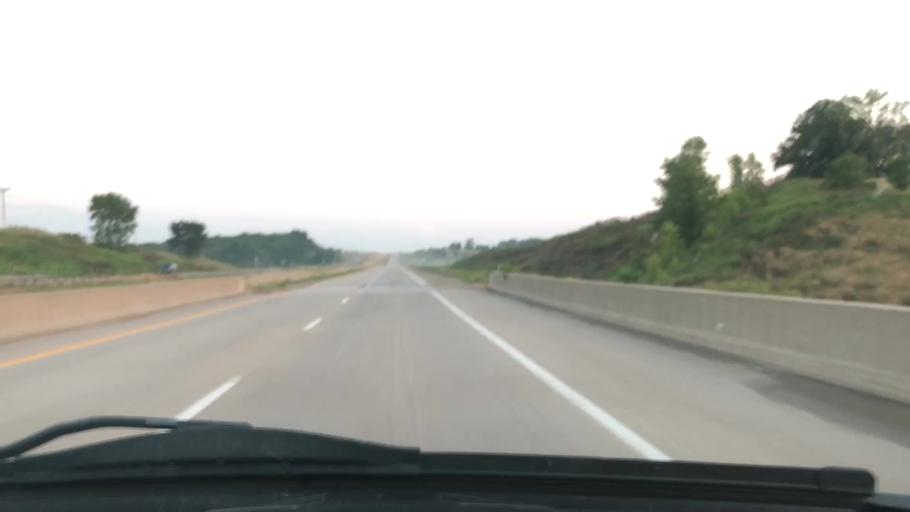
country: US
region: Iowa
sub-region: Henry County
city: Mount Pleasant
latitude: 40.8618
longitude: -91.5651
